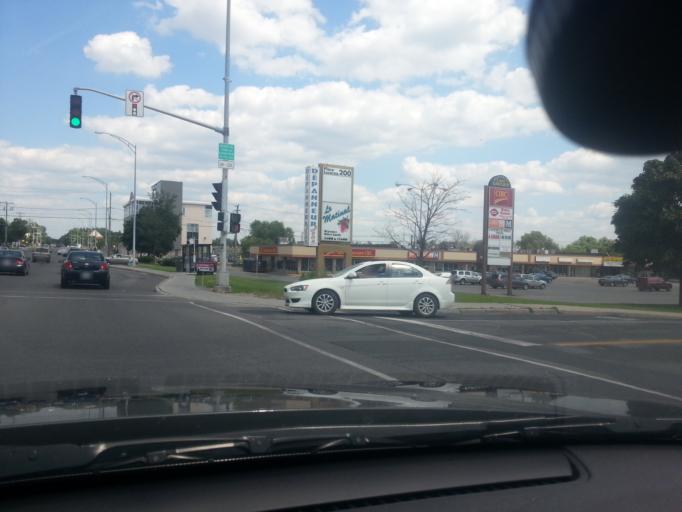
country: CA
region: Ontario
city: Bells Corners
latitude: 45.3954
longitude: -75.8356
